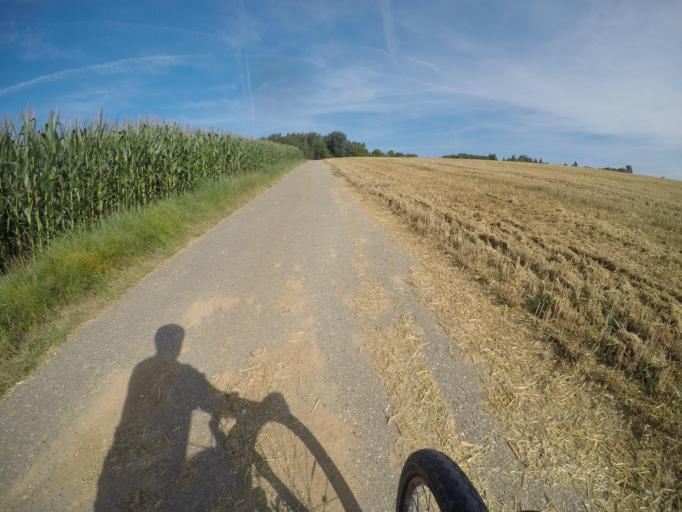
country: DE
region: Baden-Wuerttemberg
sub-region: Regierungsbezirk Stuttgart
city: Weissach
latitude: 48.8549
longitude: 8.9328
